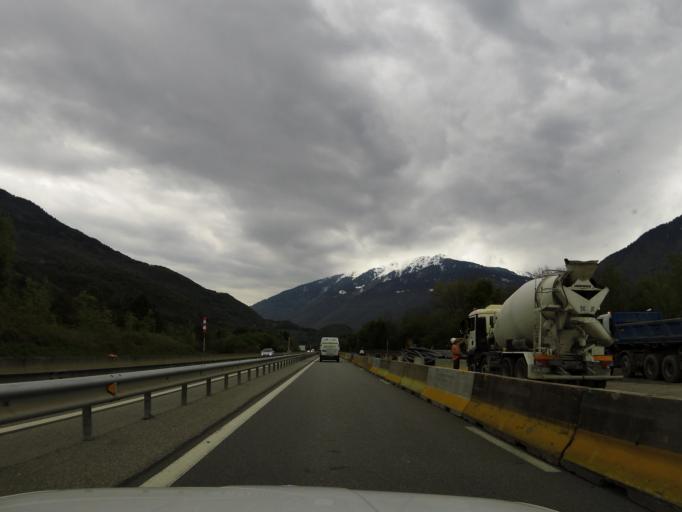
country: FR
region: Rhone-Alpes
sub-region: Departement de la Savoie
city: Aiton
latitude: 45.4872
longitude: 6.2939
